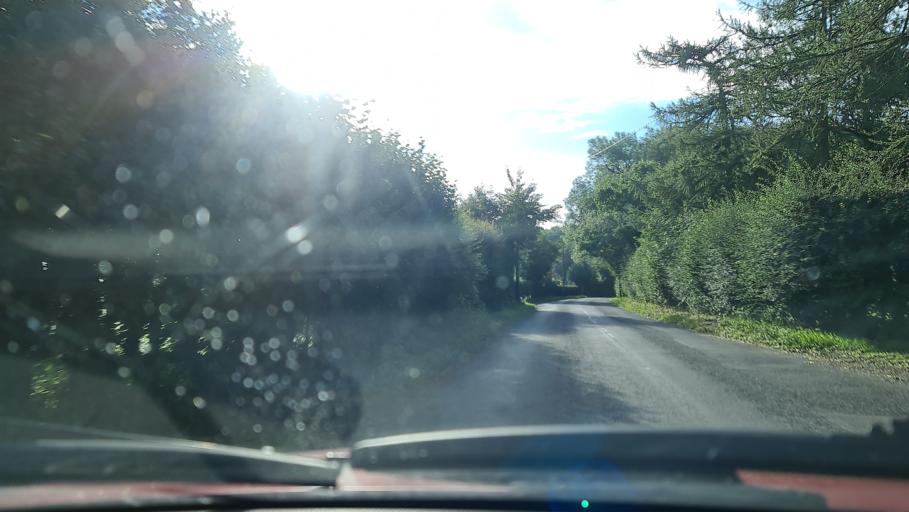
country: GB
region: England
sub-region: Oxfordshire
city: Chinnor
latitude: 51.6881
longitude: -0.8903
